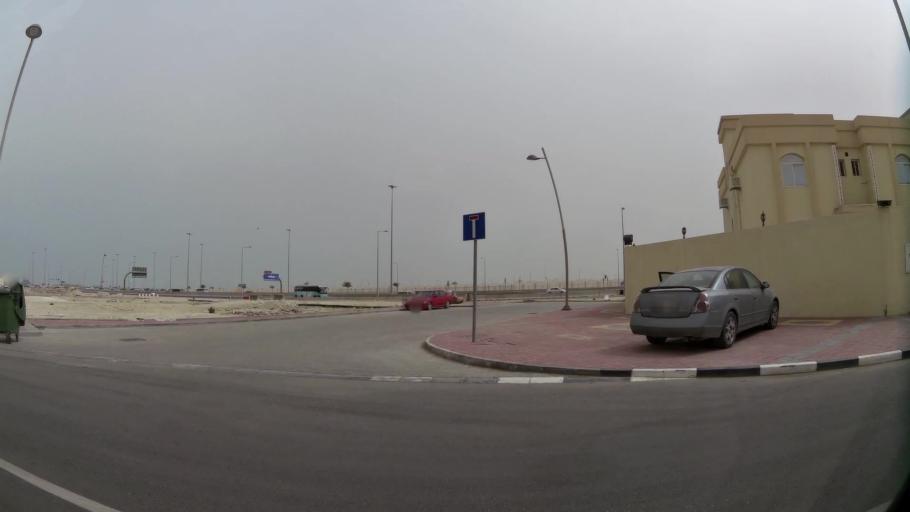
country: QA
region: Baladiyat ad Dawhah
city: Doha
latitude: 25.2267
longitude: 51.5529
